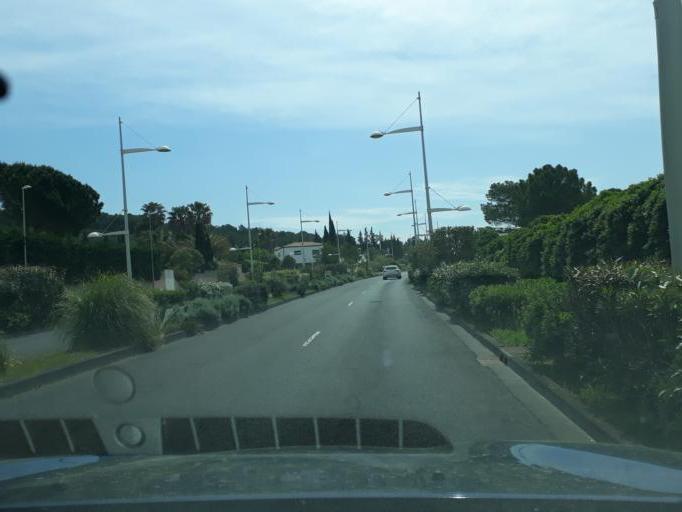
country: FR
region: Languedoc-Roussillon
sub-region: Departement de l'Herault
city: Agde
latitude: 43.2989
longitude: 3.4931
